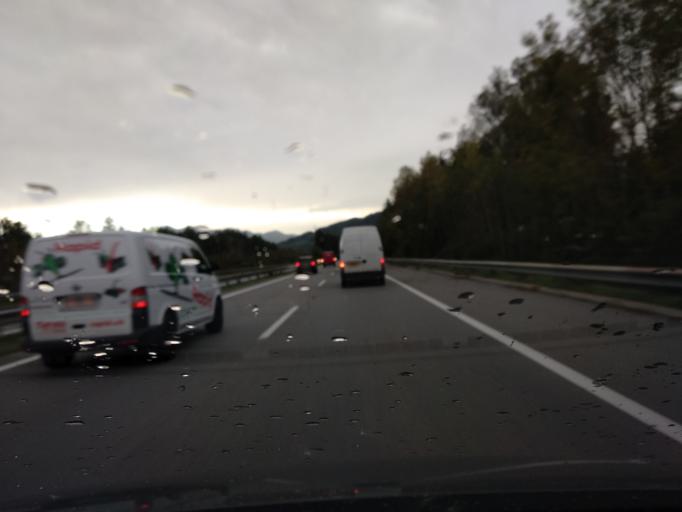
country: AT
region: Vorarlberg
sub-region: Politischer Bezirk Feldkirch
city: Satteins
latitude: 47.2120
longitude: 9.6632
